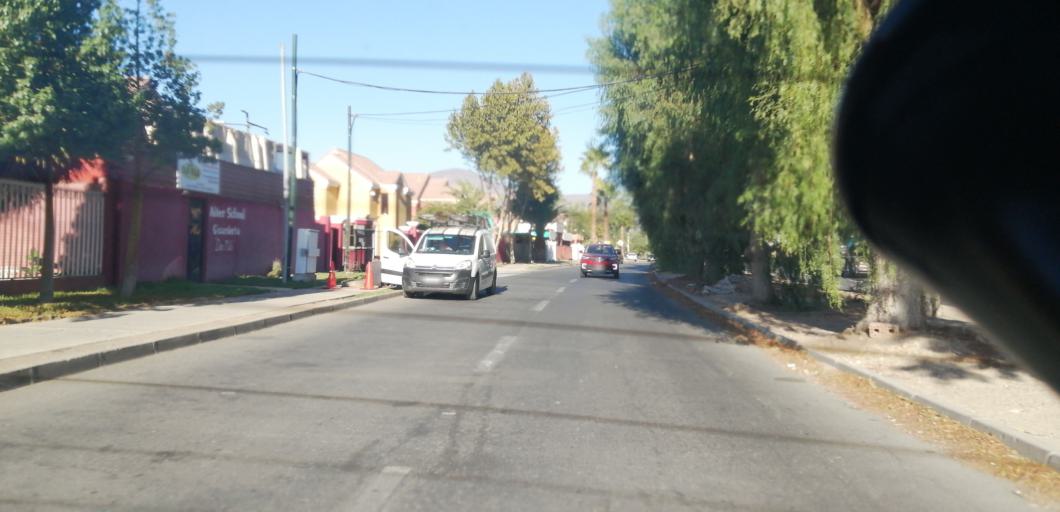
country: CL
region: Santiago Metropolitan
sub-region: Provincia de Santiago
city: Lo Prado
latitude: -33.4491
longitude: -70.8437
